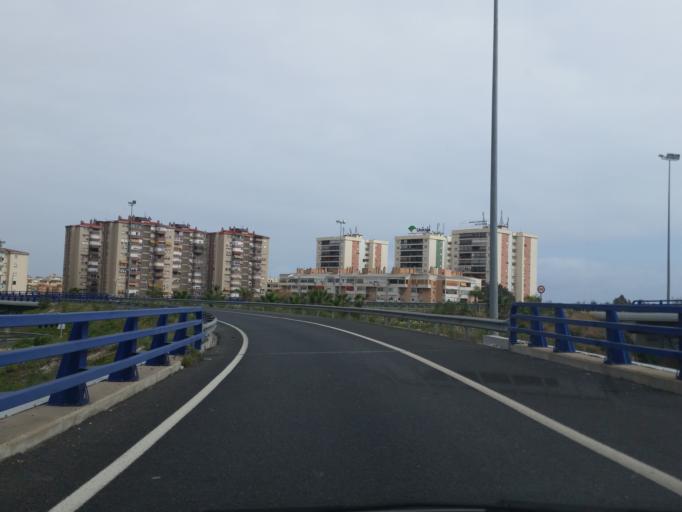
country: ES
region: Andalusia
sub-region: Provincia de Malaga
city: Malaga
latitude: 36.7116
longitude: -4.4597
